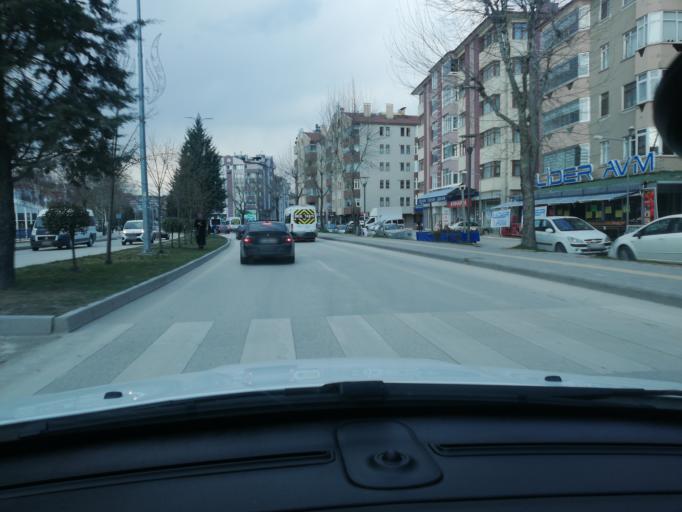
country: TR
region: Kastamonu
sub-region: Cide
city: Kastamonu
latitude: 41.3952
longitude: 33.7821
